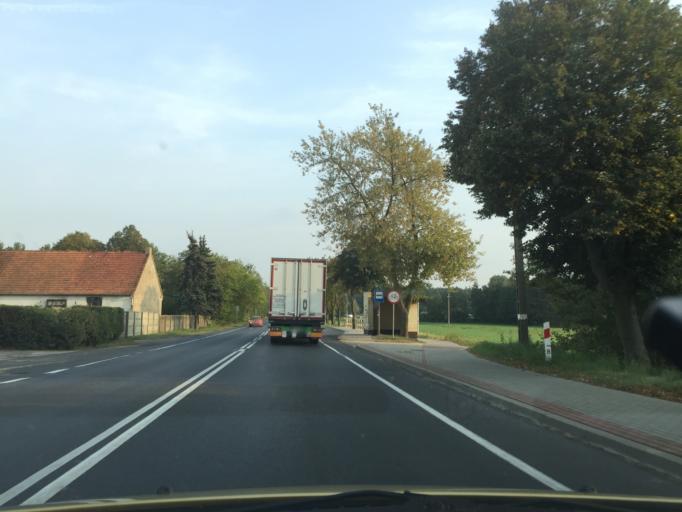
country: PL
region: Greater Poland Voivodeship
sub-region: Powiat jarocinski
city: Jarocin
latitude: 51.9989
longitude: 17.4787
